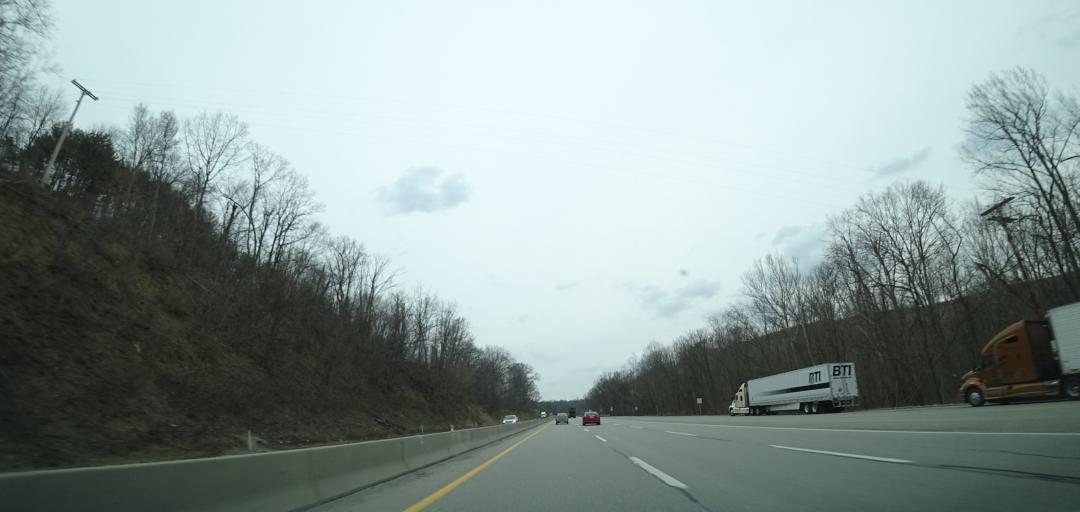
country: US
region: Pennsylvania
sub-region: Beaver County
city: West Mayfield
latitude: 40.8096
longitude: -80.3140
